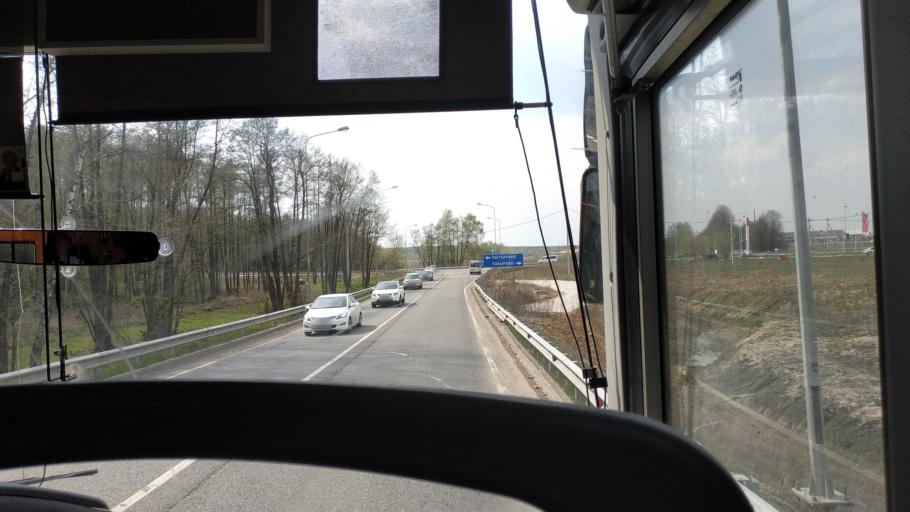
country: RU
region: Moskovskaya
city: Tomilino
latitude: 55.6212
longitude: 37.9265
